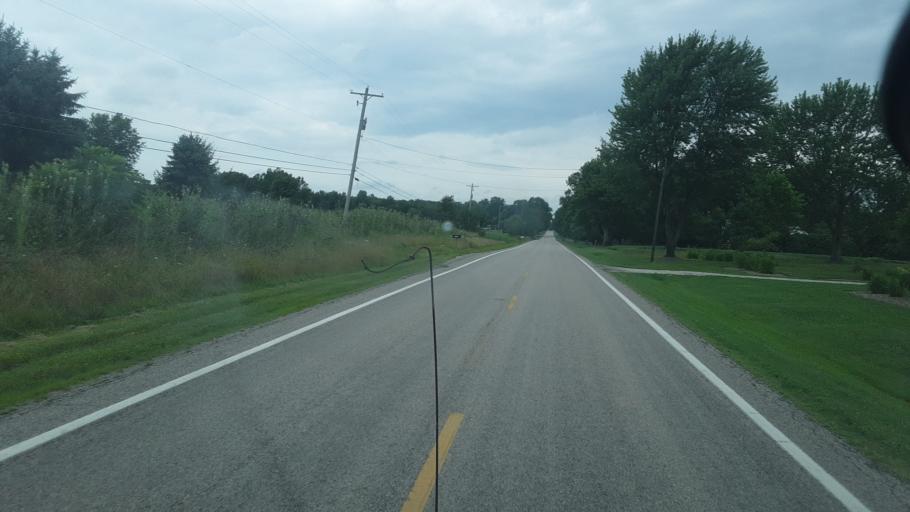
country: US
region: Ohio
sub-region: Trumbull County
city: Cortland
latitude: 41.3589
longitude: -80.6656
